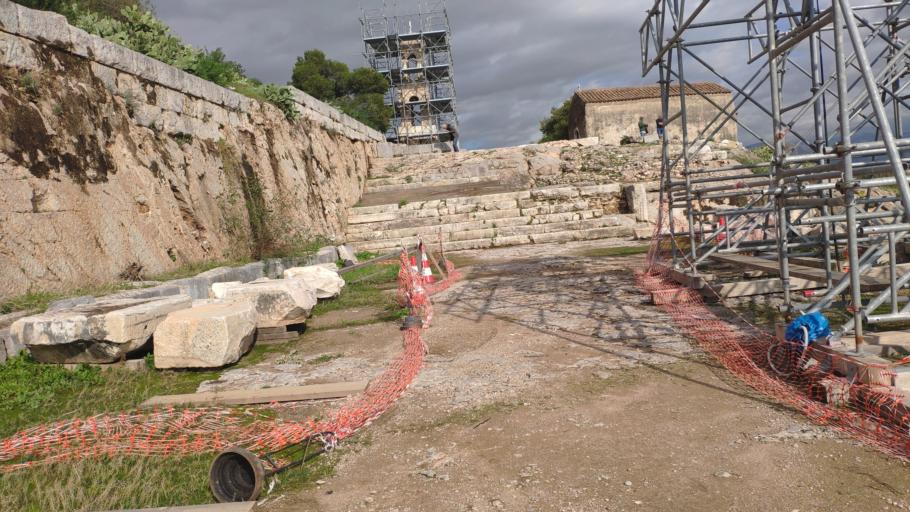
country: GR
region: Attica
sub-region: Nomarchia Dytikis Attikis
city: Elefsina
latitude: 38.0410
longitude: 23.5382
